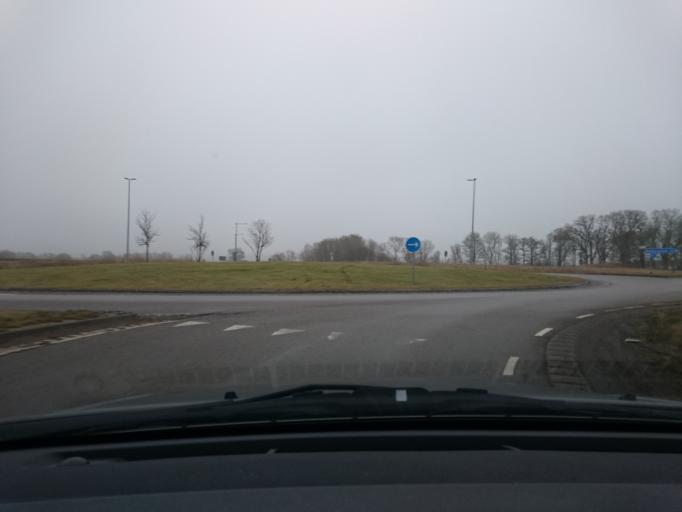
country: SE
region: Skane
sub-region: Bastads Kommun
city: Forslov
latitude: 56.3196
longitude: 12.8876
